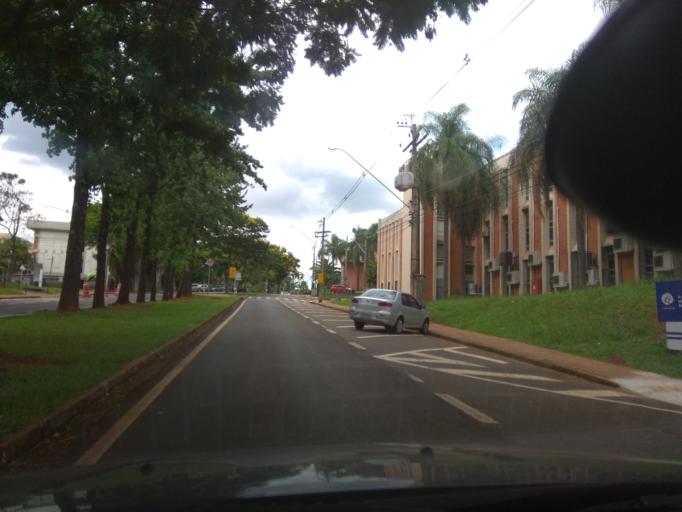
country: BR
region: Sao Paulo
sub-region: Campinas
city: Campinas
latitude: -22.8201
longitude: -47.0657
